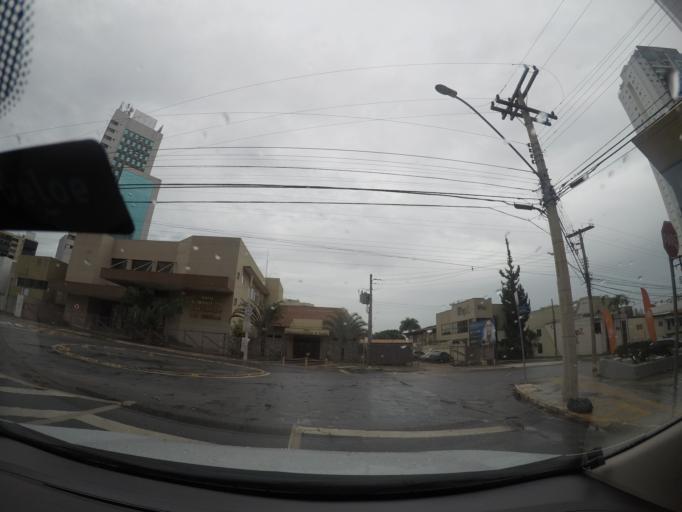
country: BR
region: Goias
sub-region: Goiania
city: Goiania
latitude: -16.6986
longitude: -49.2545
